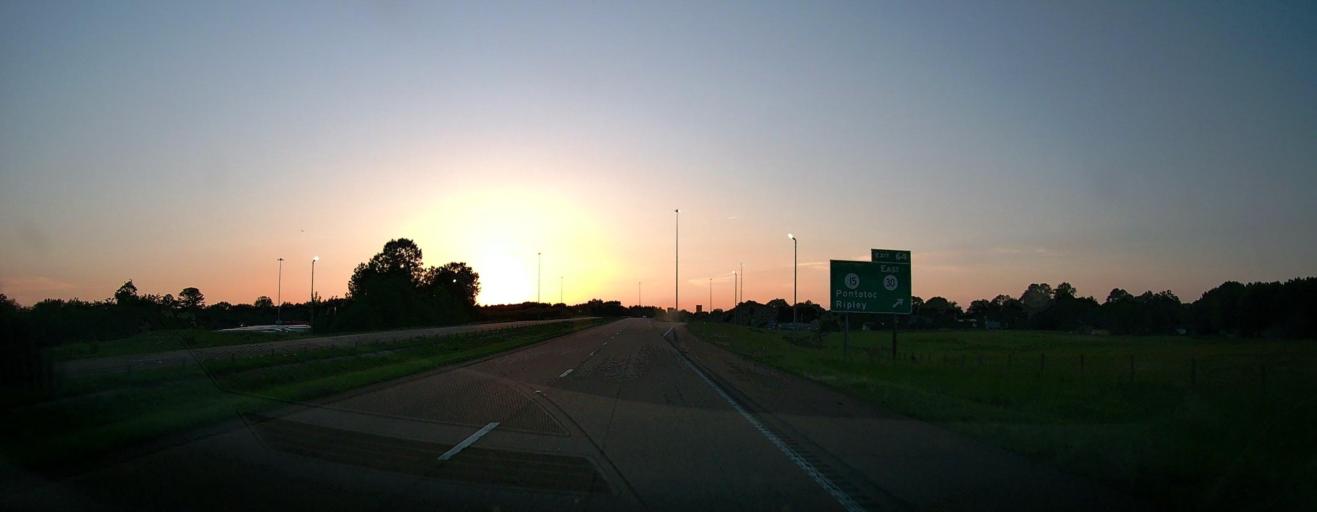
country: US
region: Mississippi
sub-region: Union County
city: New Albany
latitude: 34.4673
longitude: -89.0019
